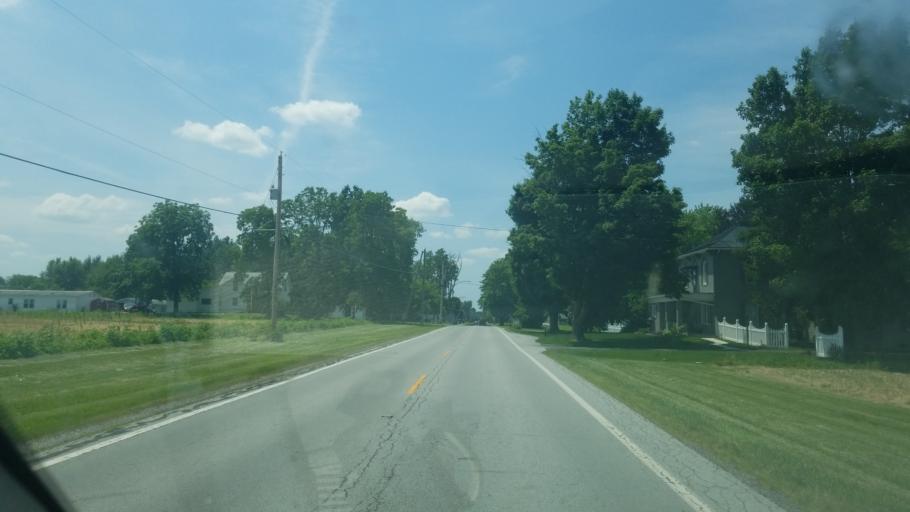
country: US
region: Ohio
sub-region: Hardin County
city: Ada
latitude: 40.7767
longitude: -83.8132
